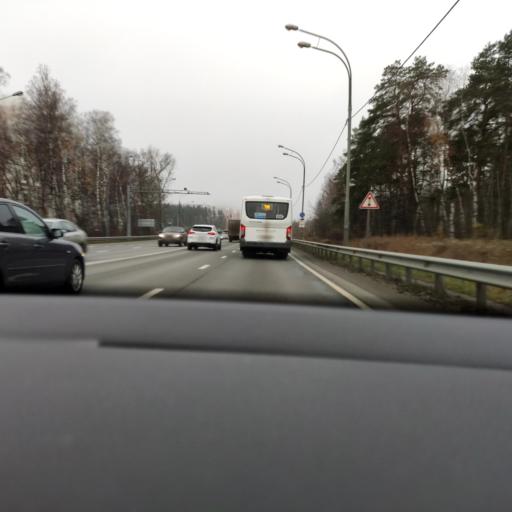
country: RU
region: Moscow
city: Vostochnyy
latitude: 55.8264
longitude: 37.8946
